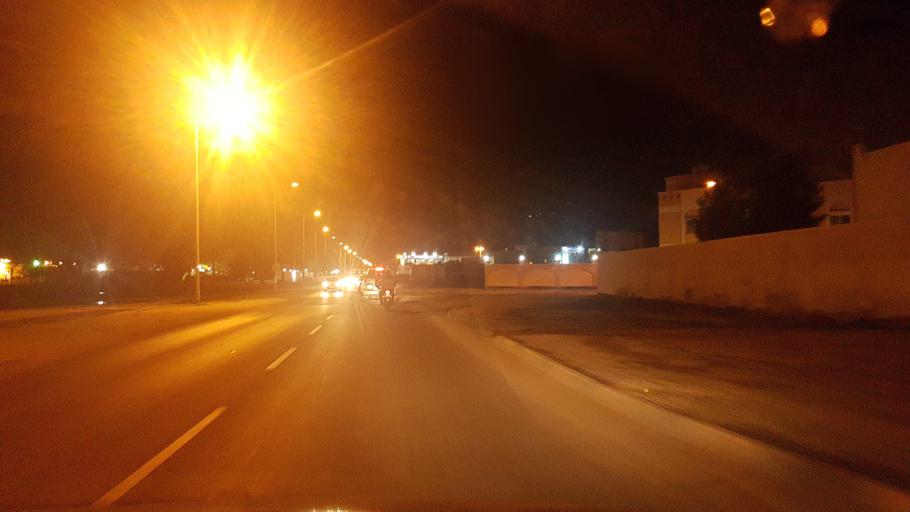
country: BH
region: Muharraq
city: Al Muharraq
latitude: 26.2762
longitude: 50.6381
